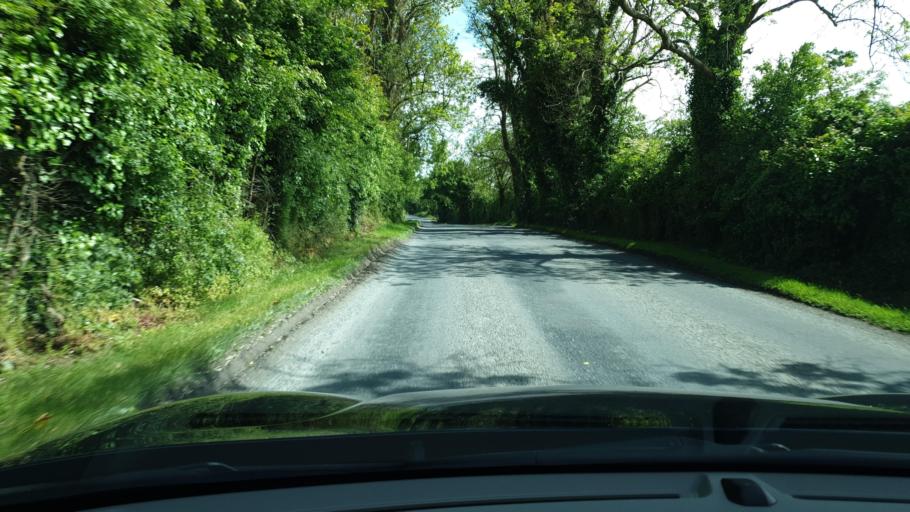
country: IE
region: Leinster
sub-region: An Mhi
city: Slane
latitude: 53.7621
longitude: -6.6112
